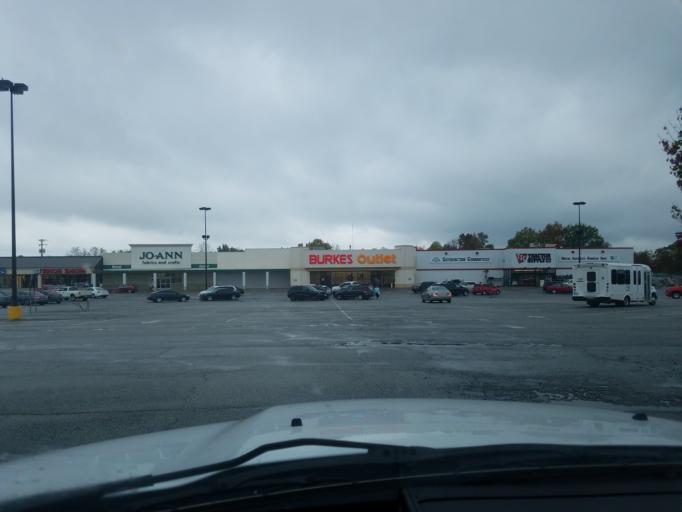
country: US
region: Kentucky
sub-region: Taylor County
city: Campbellsville
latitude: 37.3440
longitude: -85.3678
